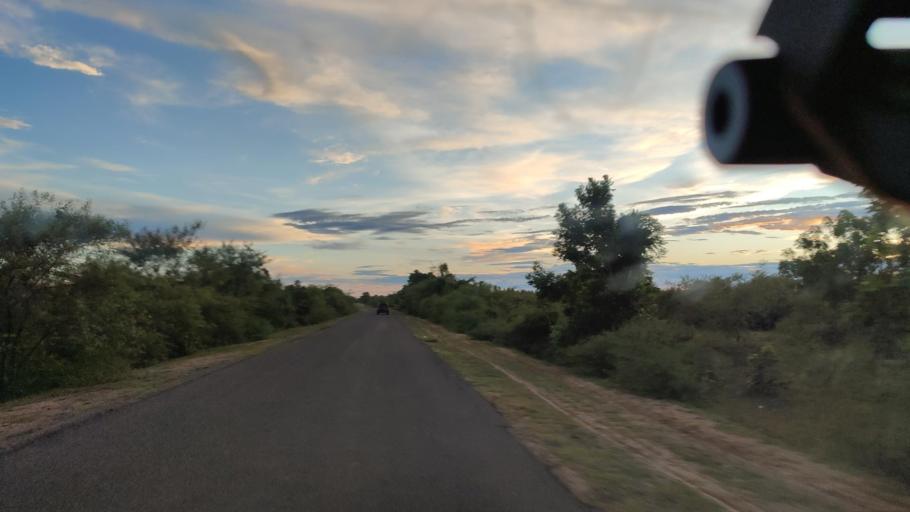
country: MM
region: Magway
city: Taungdwingyi
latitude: 20.1527
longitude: 95.5300
